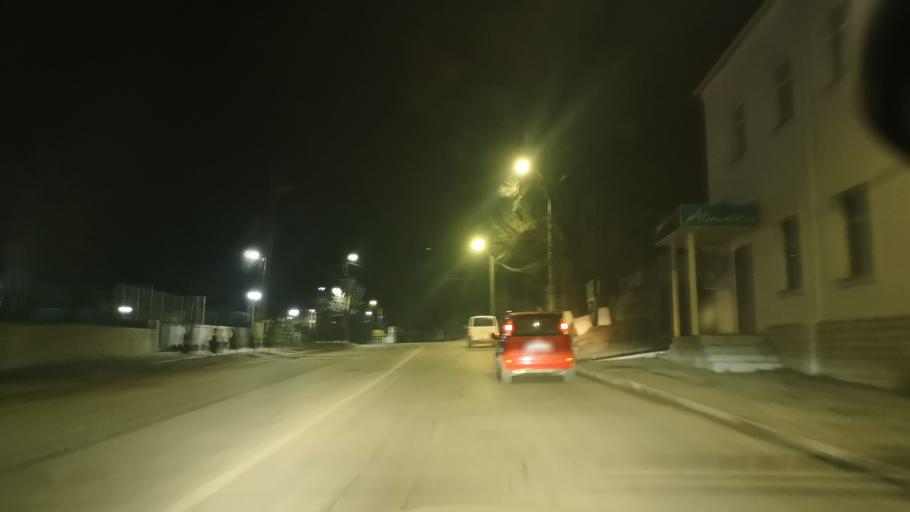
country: MD
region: Orhei
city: Orhei
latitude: 47.3654
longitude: 28.8123
